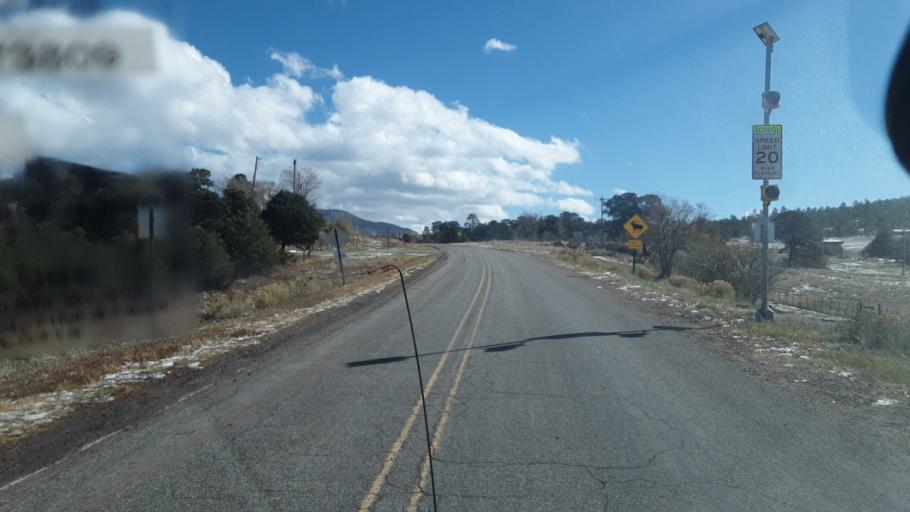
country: US
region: New Mexico
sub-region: Rio Arriba County
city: Santa Teresa
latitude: 36.2289
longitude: -106.8262
